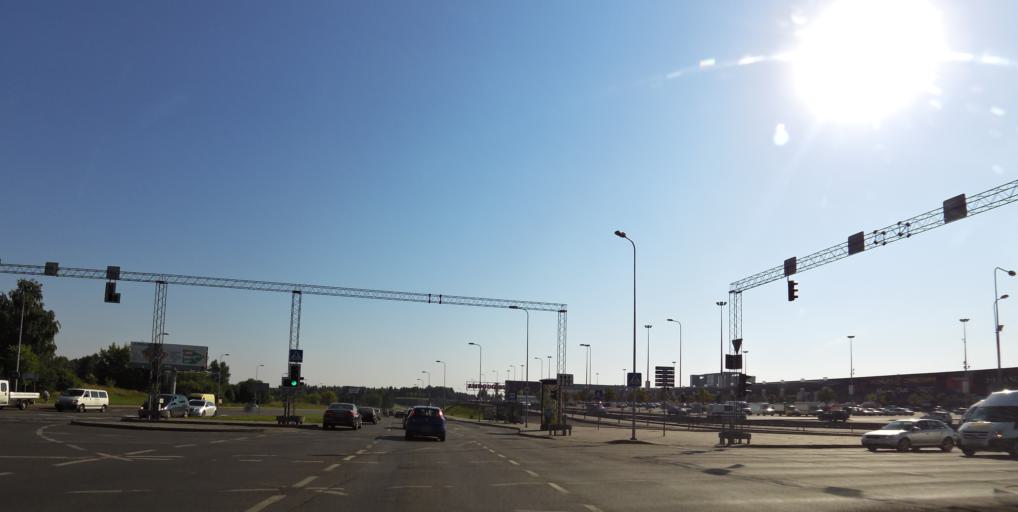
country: LT
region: Vilnius County
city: Seskine
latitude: 54.7108
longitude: 25.2572
